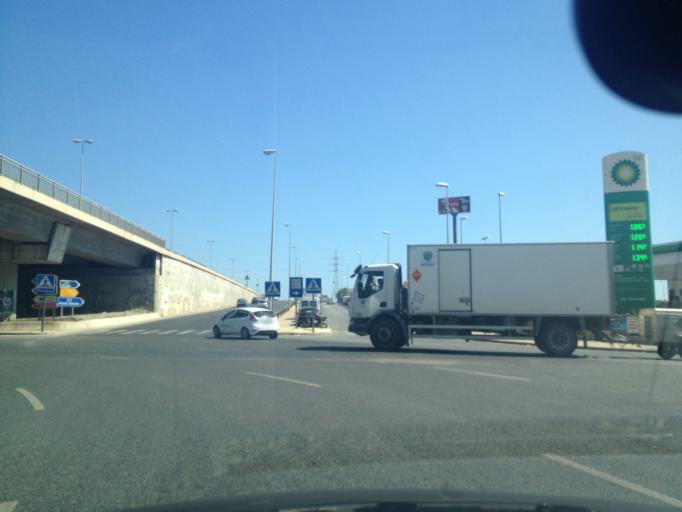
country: ES
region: Andalusia
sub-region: Provincia de Malaga
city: Malaga
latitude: 36.7133
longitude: -4.4732
